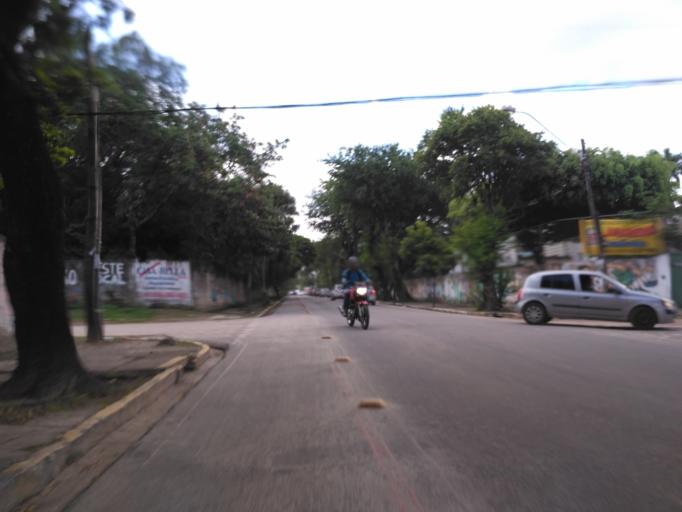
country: BR
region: Pernambuco
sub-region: Recife
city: Recife
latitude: -8.0542
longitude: -34.9417
